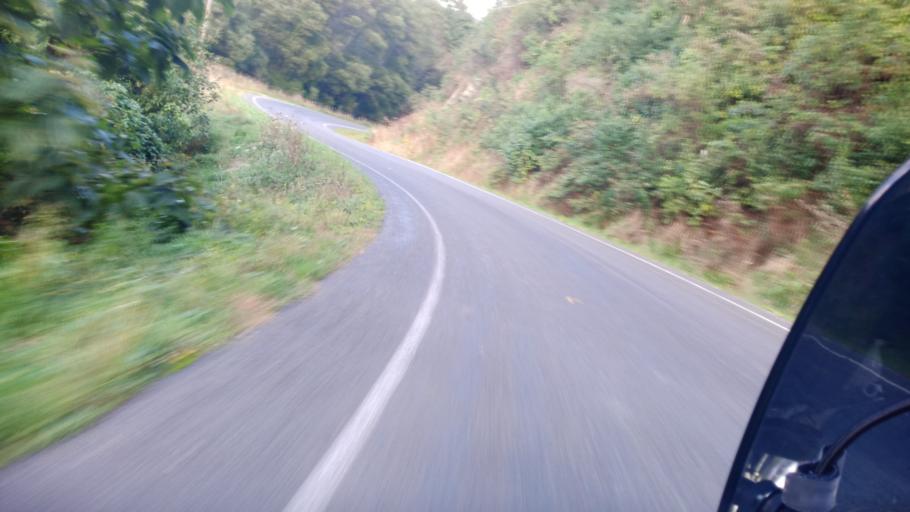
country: NZ
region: Gisborne
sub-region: Gisborne District
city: Gisborne
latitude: -38.5300
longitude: 177.5424
